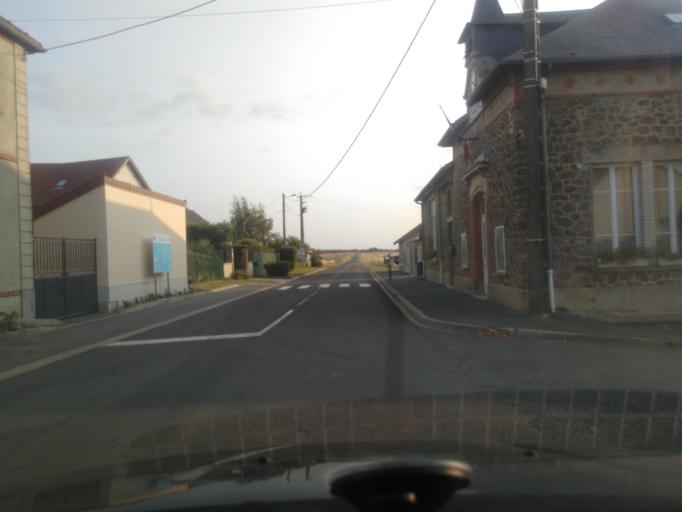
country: FR
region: Champagne-Ardenne
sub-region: Departement de la Marne
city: Chatillon-sur-Marne
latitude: 49.1479
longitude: 3.7583
